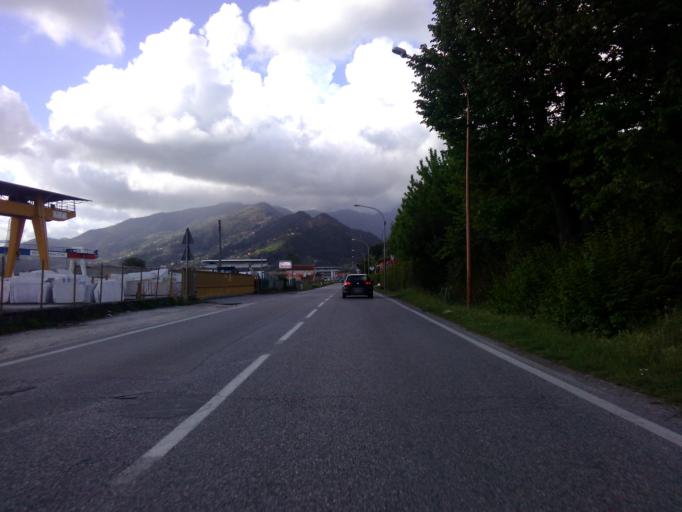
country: IT
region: Tuscany
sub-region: Provincia di Lucca
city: Ripa-Pozzi-Querceta-Ponterosso
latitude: 43.9698
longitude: 10.2206
